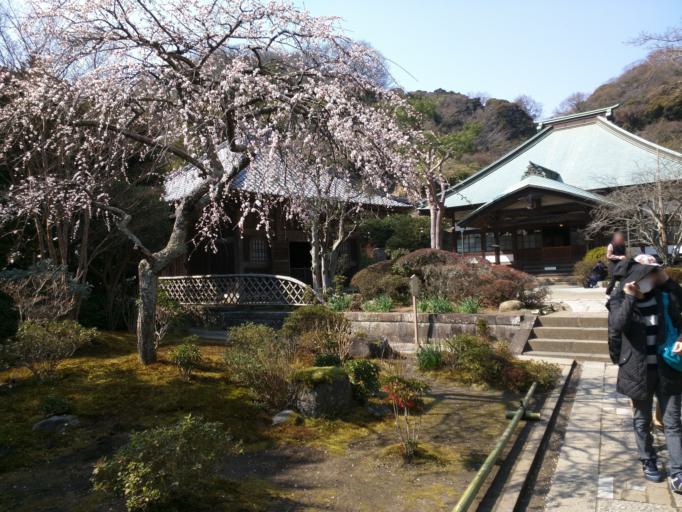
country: JP
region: Kanagawa
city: Kamakura
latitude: 35.3287
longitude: 139.5456
